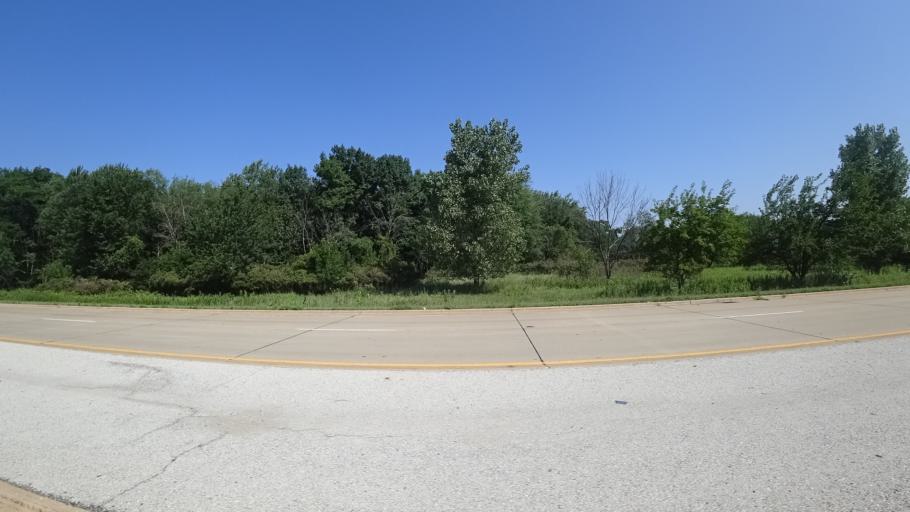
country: US
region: Illinois
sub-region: Cook County
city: Matteson
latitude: 41.5279
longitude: -87.7549
